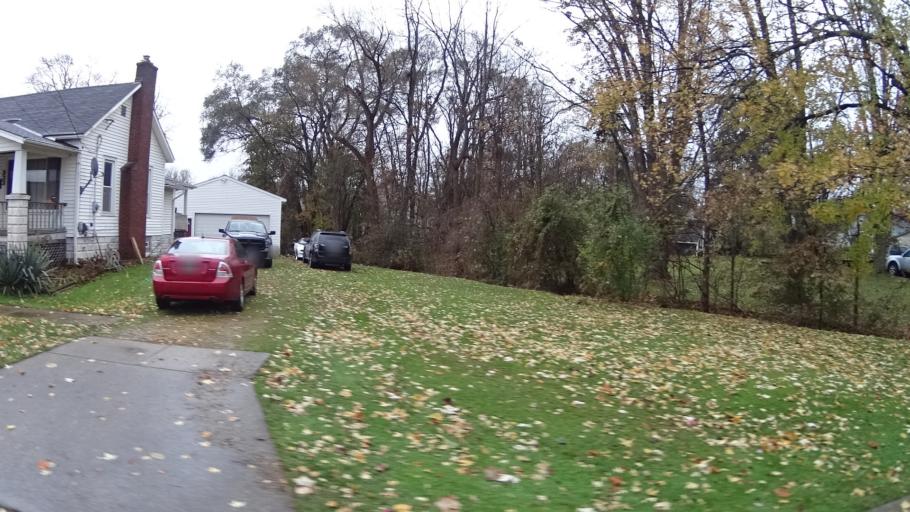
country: US
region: Ohio
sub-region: Lorain County
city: Elyria
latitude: 41.3817
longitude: -82.1238
